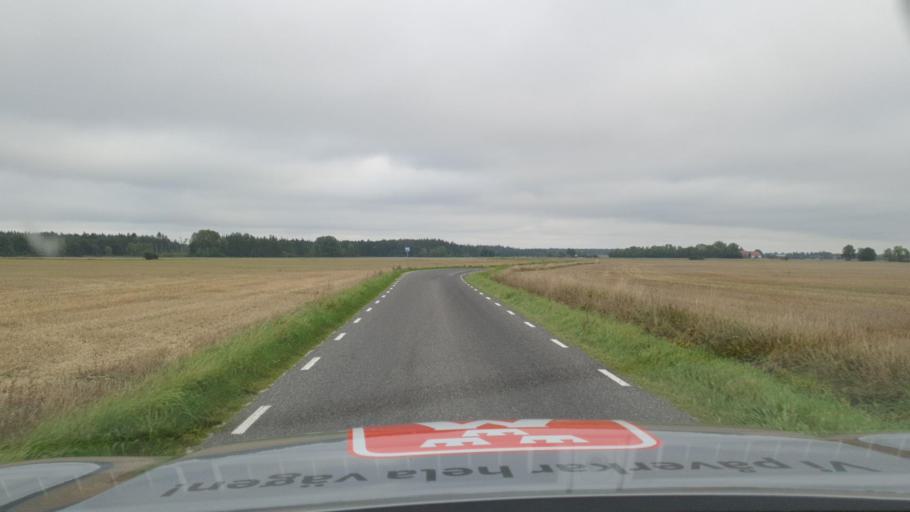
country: SE
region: Gotland
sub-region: Gotland
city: Visby
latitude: 57.6305
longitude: 18.4715
